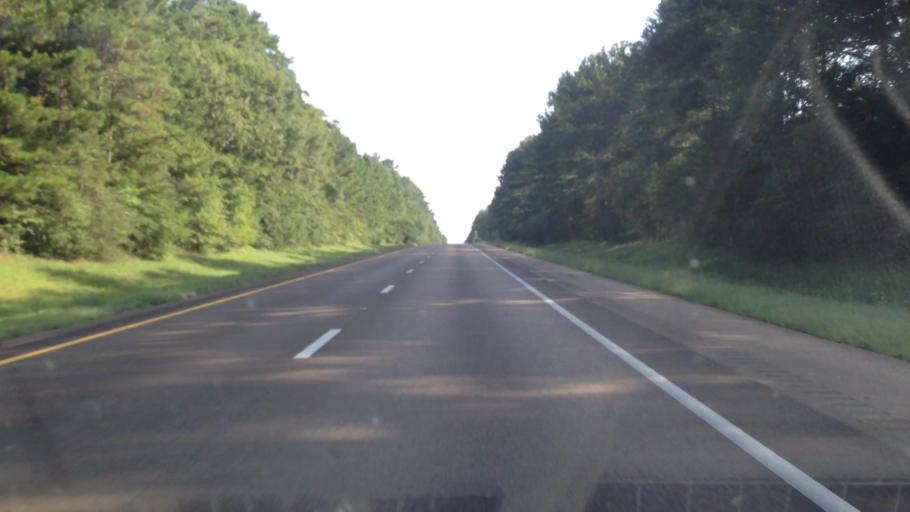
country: US
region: Mississippi
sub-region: Pike County
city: Summit
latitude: 31.3977
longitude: -90.4792
